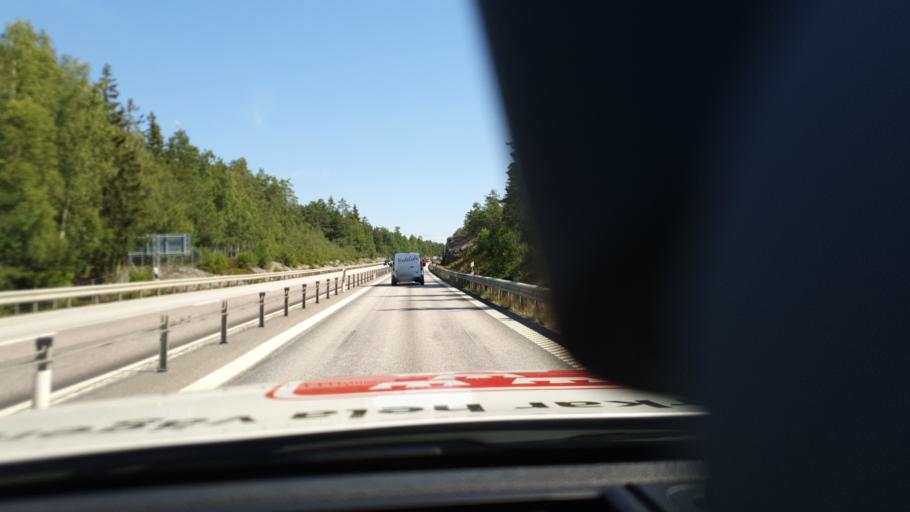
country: SE
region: Stockholm
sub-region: Norrtalje Kommun
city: Rimbo
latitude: 59.6289
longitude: 18.3178
